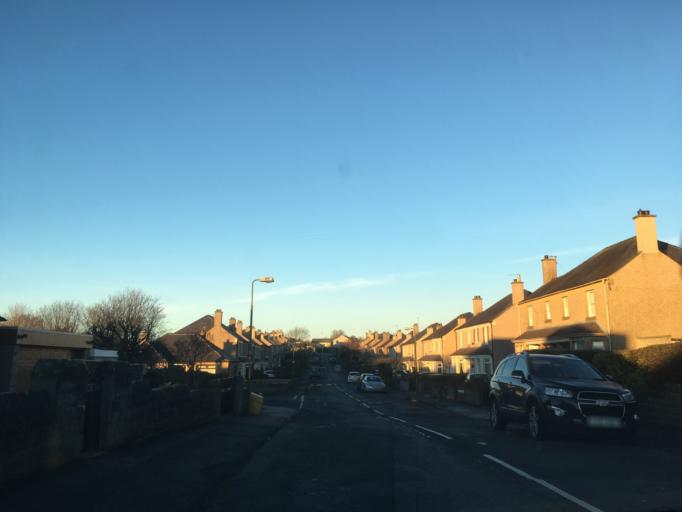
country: GB
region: Scotland
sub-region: Edinburgh
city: Currie
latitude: 55.9431
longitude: -3.3015
